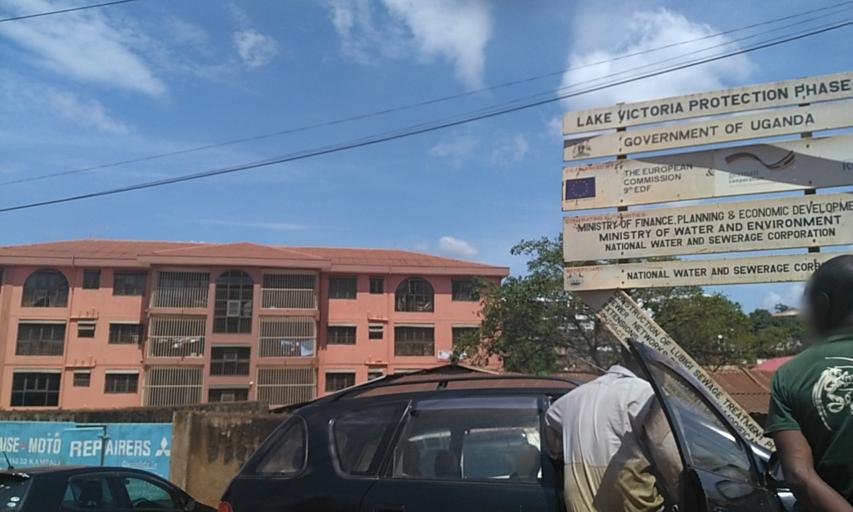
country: UG
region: Central Region
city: Kampala Central Division
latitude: 0.3361
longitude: 32.5732
